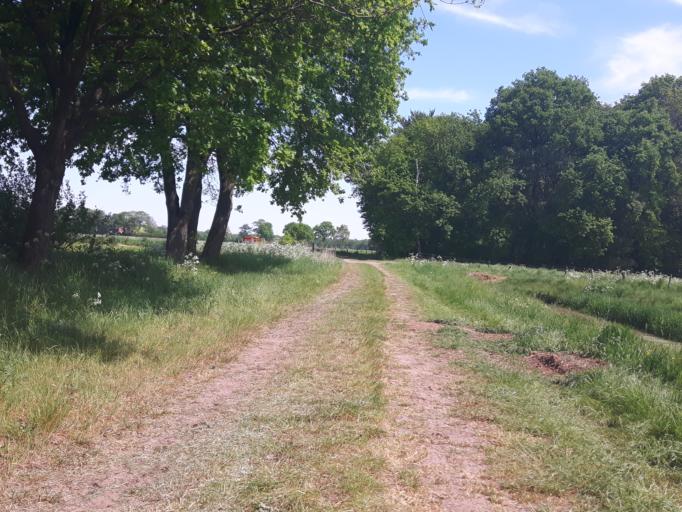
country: NL
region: Overijssel
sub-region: Gemeente Enschede
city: Enschede
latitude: 52.1634
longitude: 6.8546
